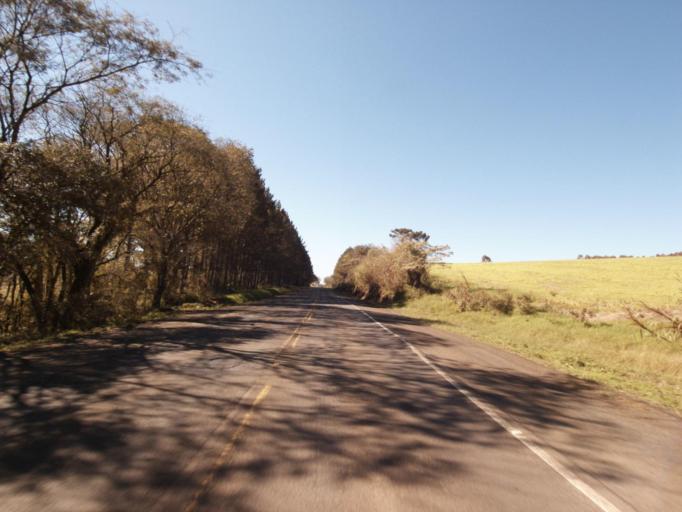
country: BR
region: Santa Catarina
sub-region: Sao Lourenco Do Oeste
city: Sao Lourenco dOeste
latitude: -26.8295
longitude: -53.1353
